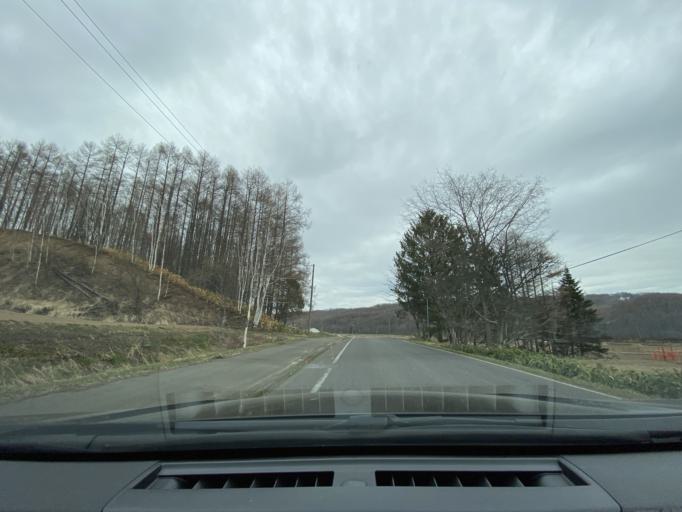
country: JP
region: Hokkaido
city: Nayoro
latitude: 44.0745
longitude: 142.4091
